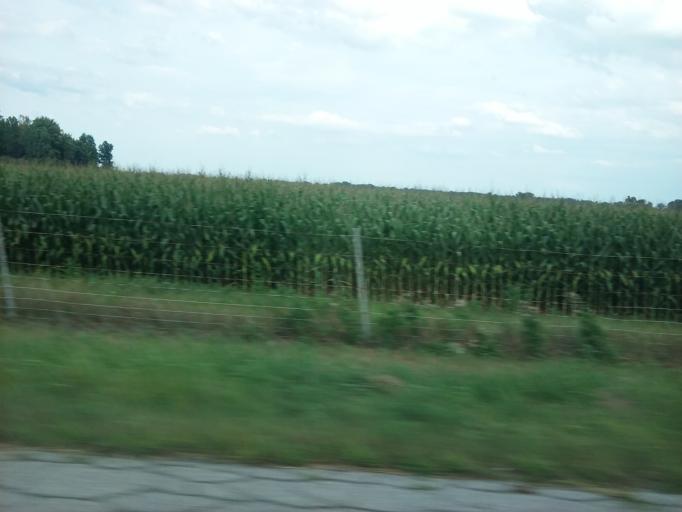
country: US
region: Ohio
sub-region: Wood County
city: Bowling Green
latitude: 41.3090
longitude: -83.6503
